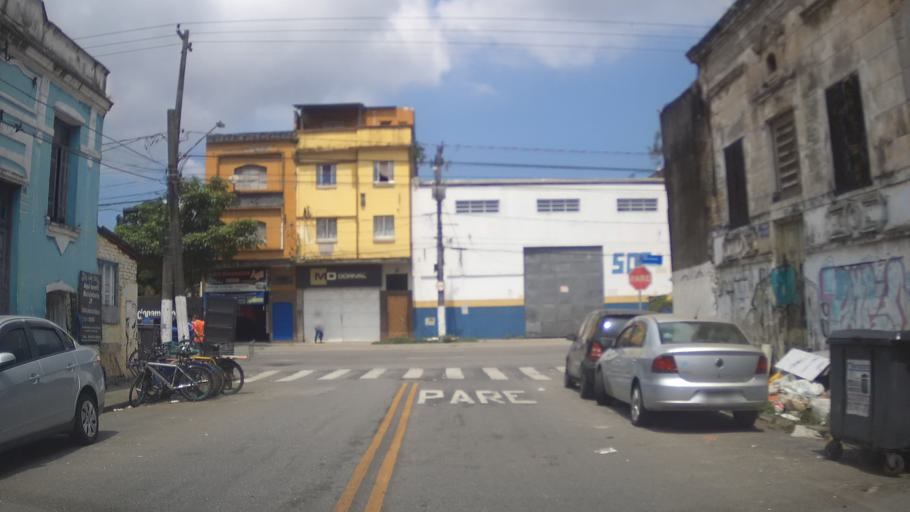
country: BR
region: Sao Paulo
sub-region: Santos
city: Santos
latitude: -23.9362
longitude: -46.3197
